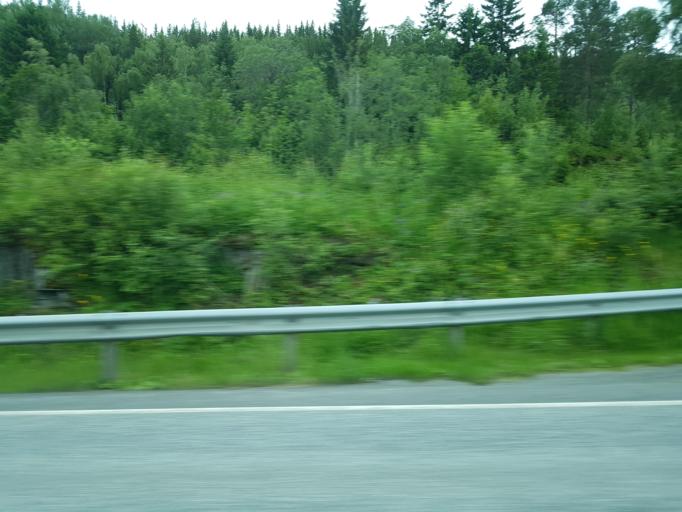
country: NO
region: Nord-Trondelag
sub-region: Stjordal
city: Stjordal
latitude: 63.5442
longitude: 10.8763
